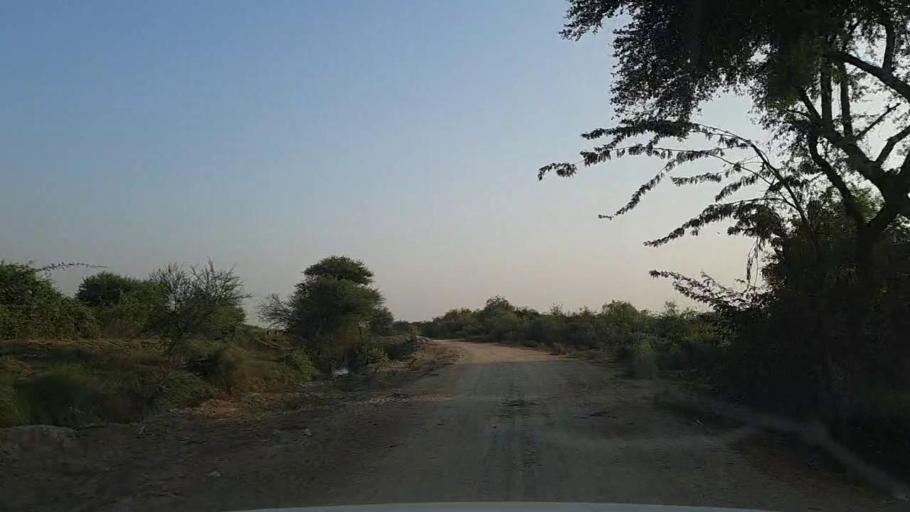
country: PK
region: Sindh
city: Daro Mehar
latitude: 24.7440
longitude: 68.1839
